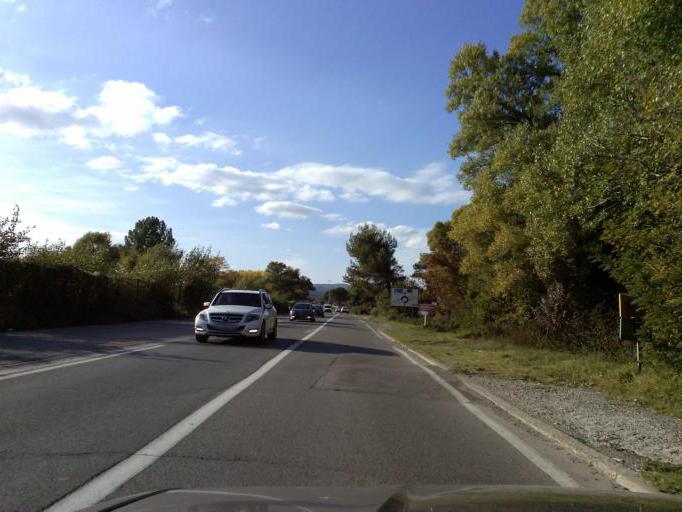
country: FR
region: Provence-Alpes-Cote d'Azur
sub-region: Departement des Alpes-de-Haute-Provence
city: Manosque
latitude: 43.8054
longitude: 5.8224
